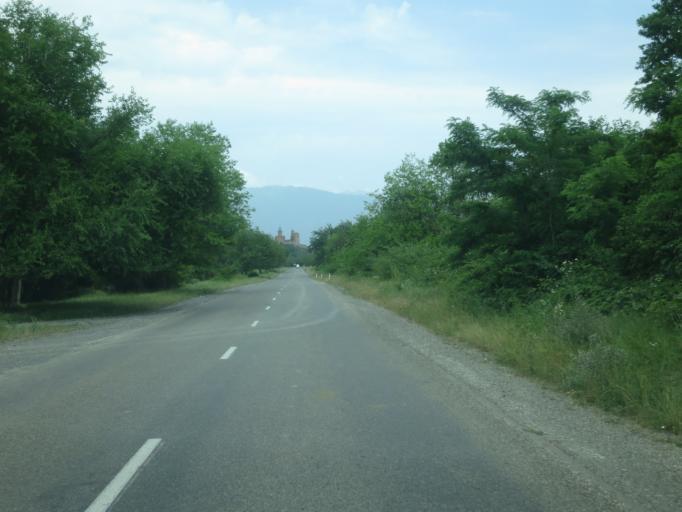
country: GE
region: Kakheti
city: Tsinandali
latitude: 41.9993
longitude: 45.6440
